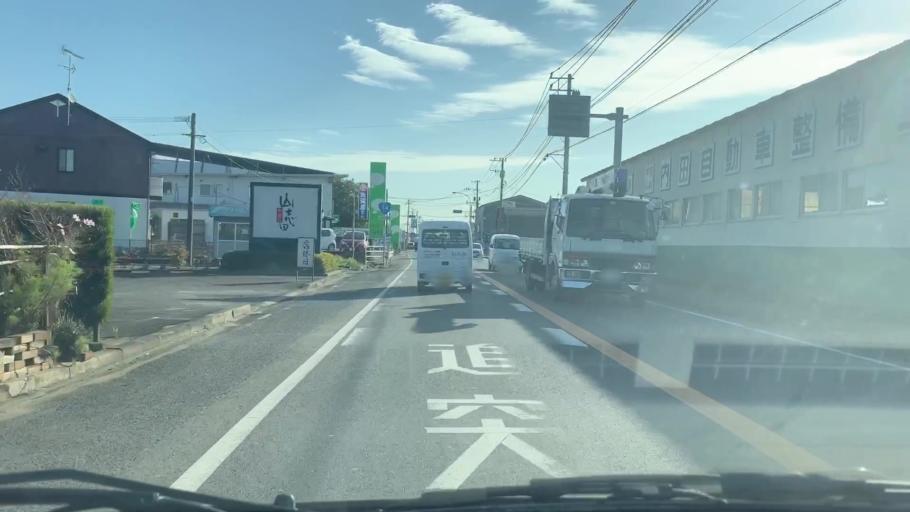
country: JP
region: Saga Prefecture
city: Takeocho-takeo
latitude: 33.2145
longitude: 130.0961
